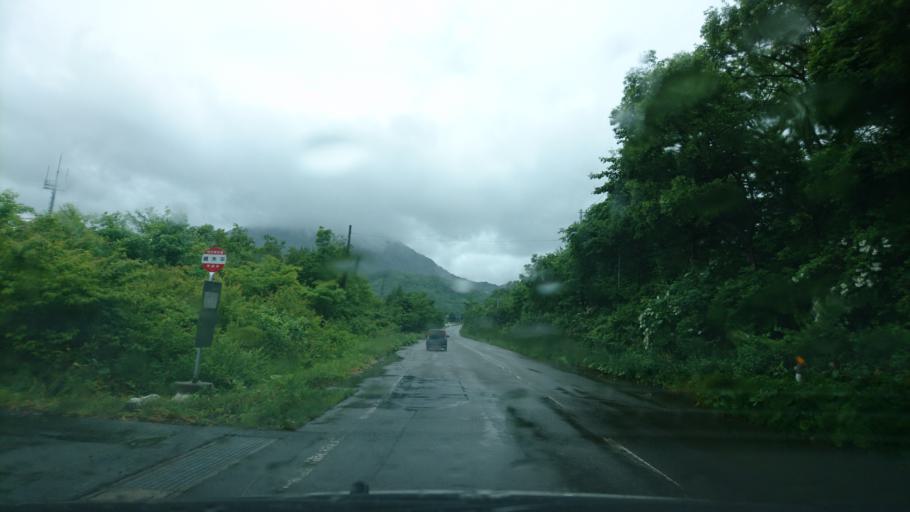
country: JP
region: Iwate
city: Ichinoseki
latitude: 39.0143
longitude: 140.8837
